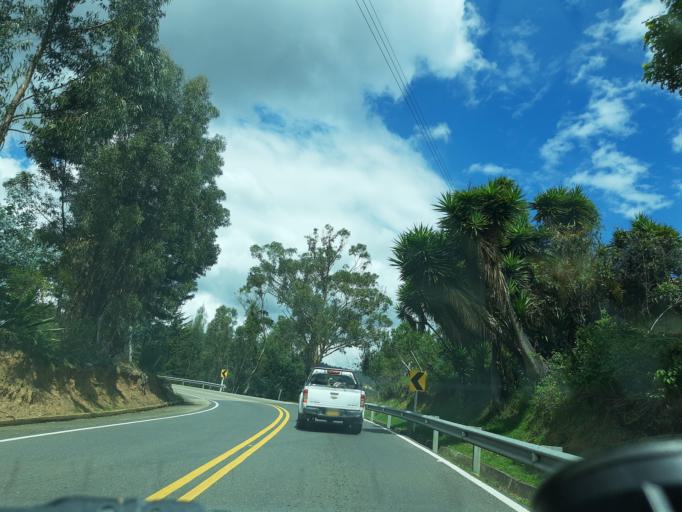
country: CO
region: Boyaca
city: Raquira
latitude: 5.5807
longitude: -73.6846
